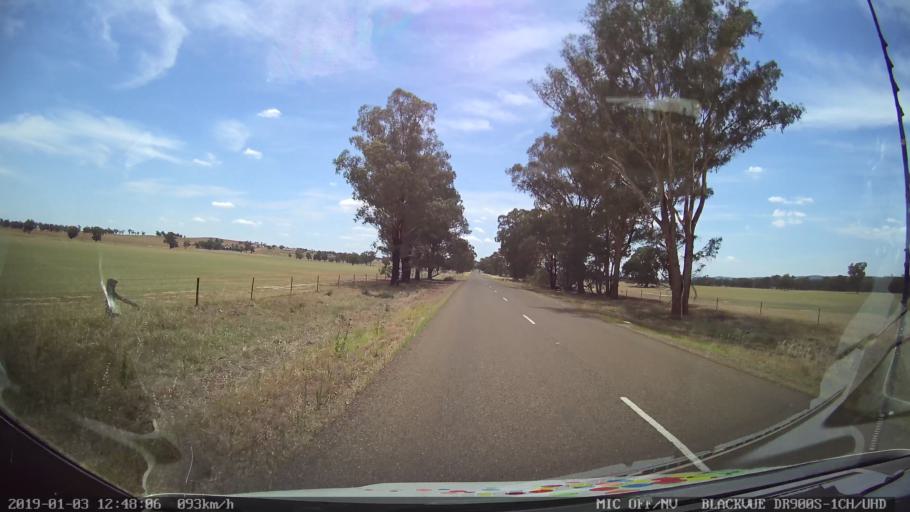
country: AU
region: New South Wales
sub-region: Weddin
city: Grenfell
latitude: -33.7186
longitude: 148.2476
